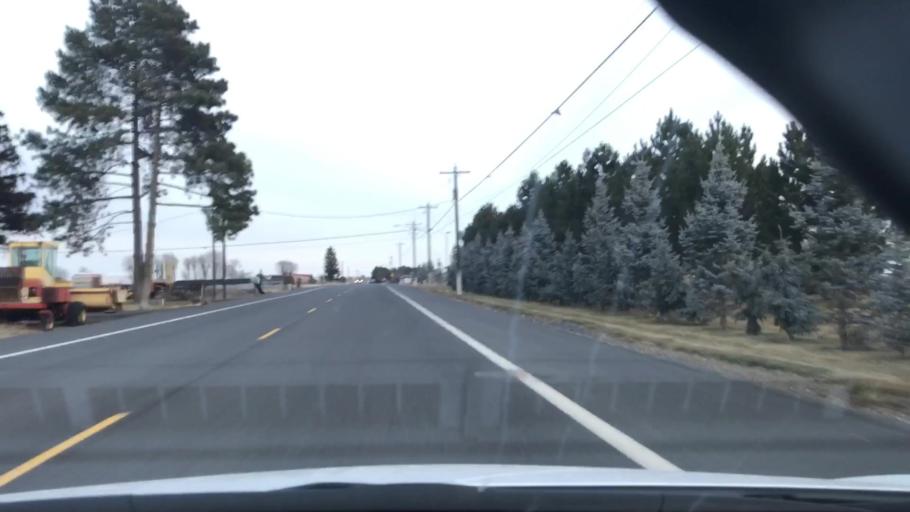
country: US
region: Washington
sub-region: Grant County
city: Moses Lake
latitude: 47.1462
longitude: -119.2435
